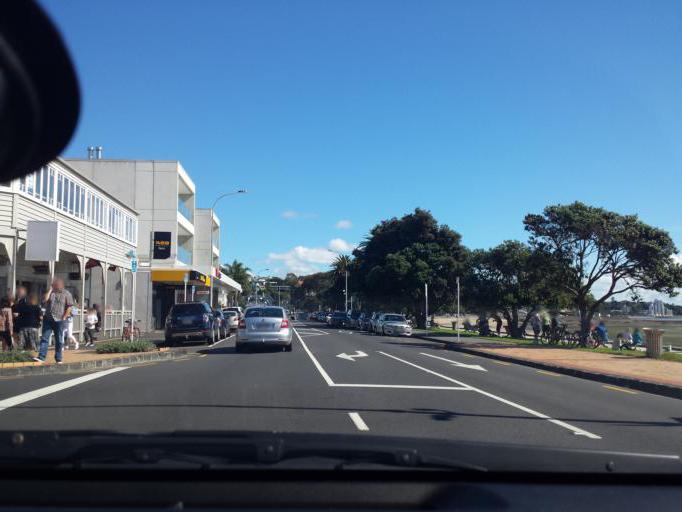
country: NZ
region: Auckland
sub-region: Auckland
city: Tamaki
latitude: -36.8503
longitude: 174.8574
